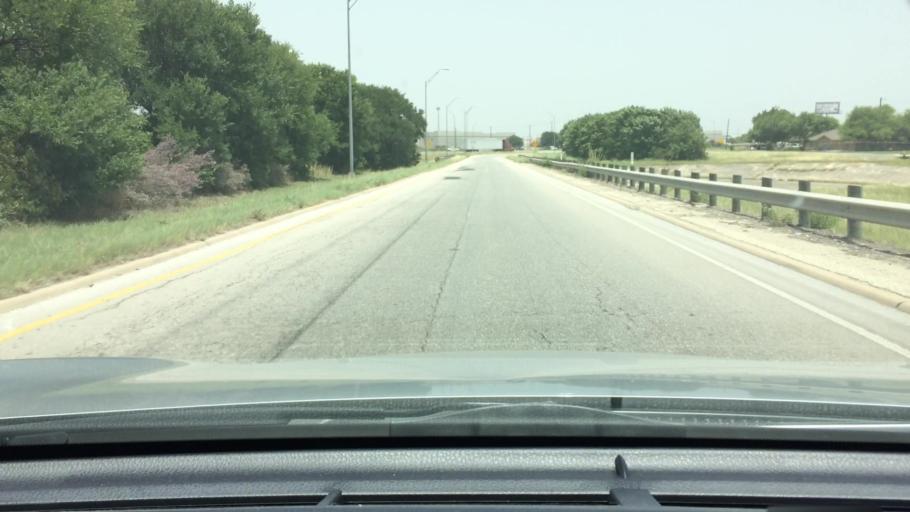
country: US
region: Texas
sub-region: Bexar County
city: Kirby
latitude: 29.4344
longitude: -98.3884
